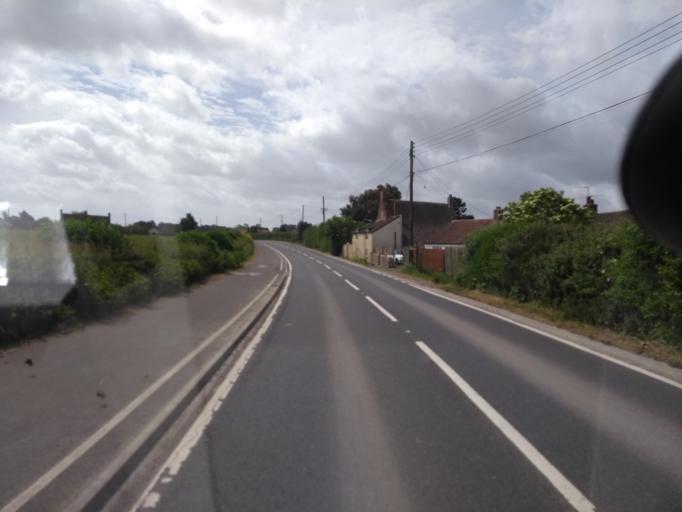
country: GB
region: England
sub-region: Somerset
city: Bridgwater
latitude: 51.1625
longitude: -3.0674
